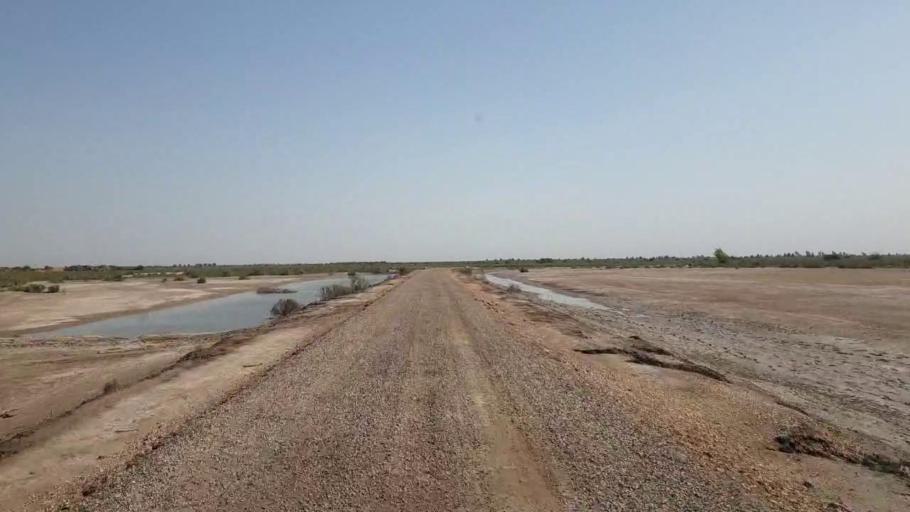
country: PK
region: Sindh
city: Tando Bago
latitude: 24.7307
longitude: 69.0304
